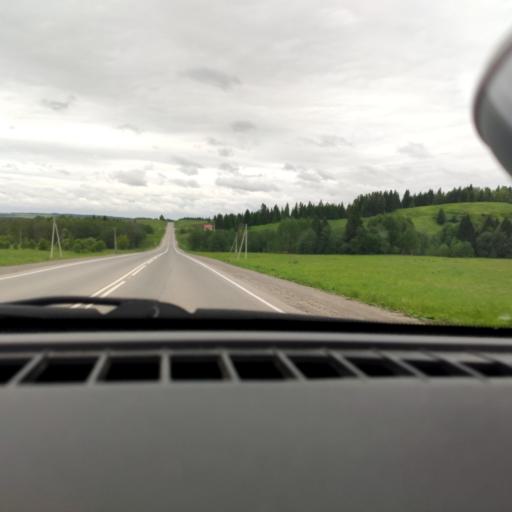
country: RU
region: Perm
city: Kultayevo
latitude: 57.8948
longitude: 55.7930
